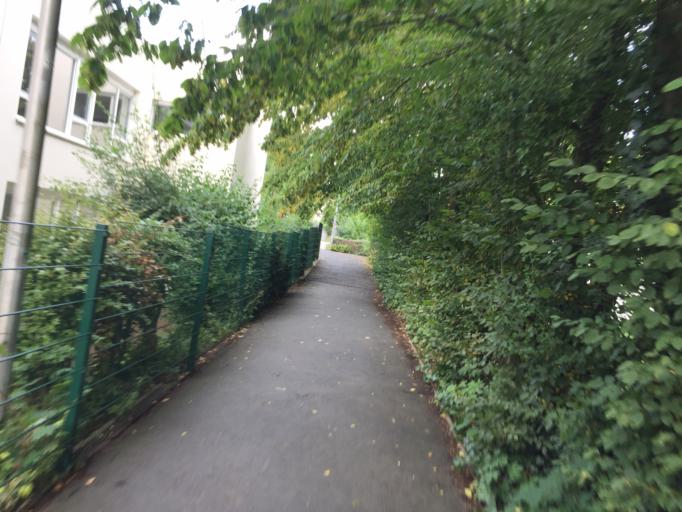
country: DE
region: Hesse
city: Schwalmstadt
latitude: 50.9172
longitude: 9.1937
